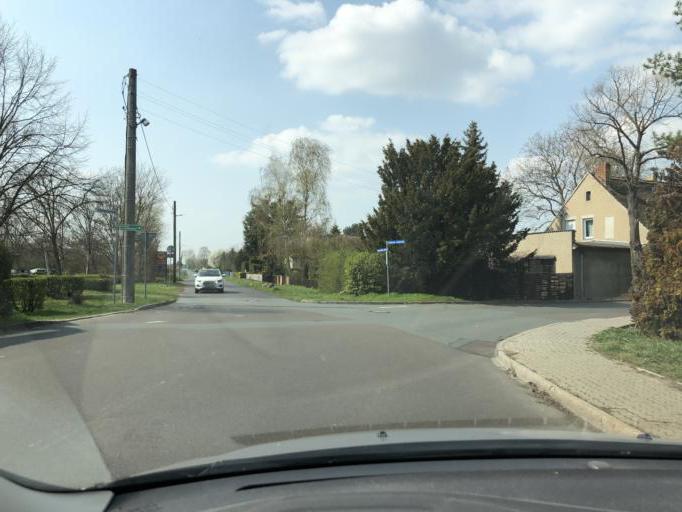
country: DE
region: Saxony-Anhalt
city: Landsberg
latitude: 51.5249
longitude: 12.1546
